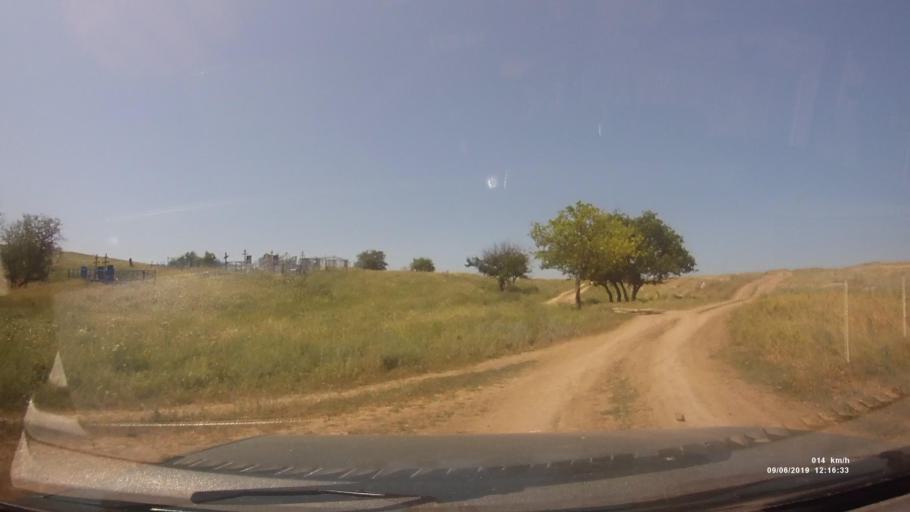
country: RU
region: Rostov
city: Staraya Stanitsa
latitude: 48.2556
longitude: 40.3193
